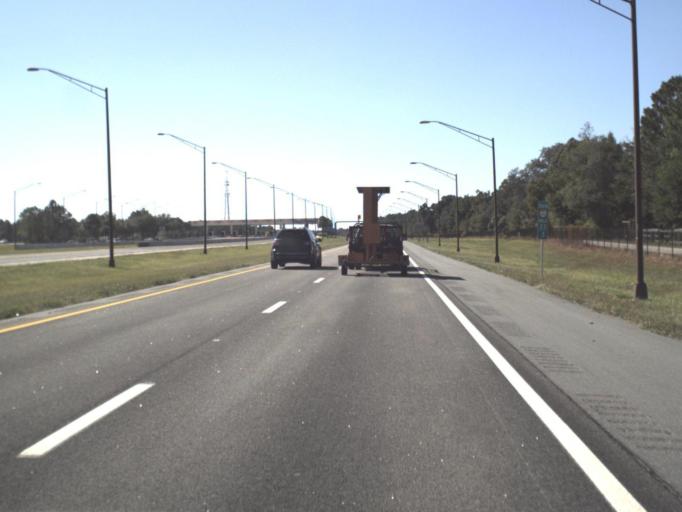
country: US
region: Florida
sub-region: Pasco County
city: Shady Hills
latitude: 28.3971
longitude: -82.5255
